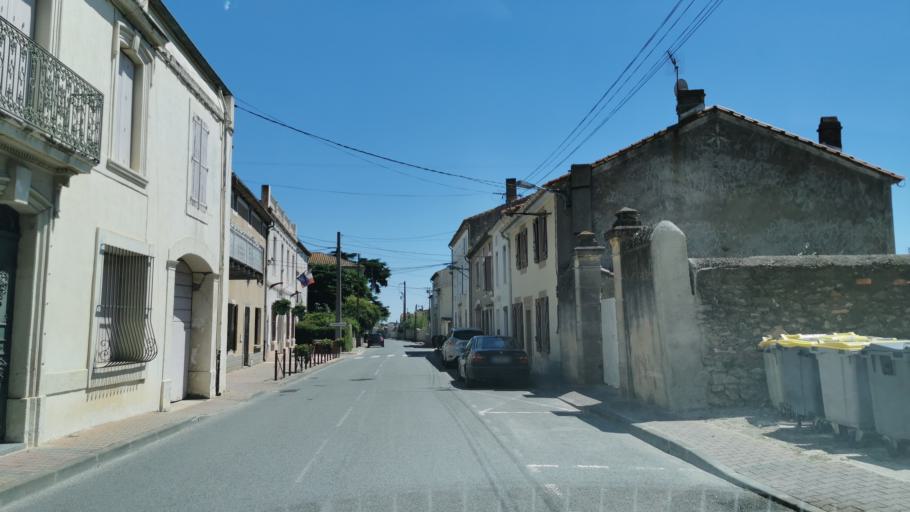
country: FR
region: Languedoc-Roussillon
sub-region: Departement de l'Aude
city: Marcorignan
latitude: 43.2441
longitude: 2.8964
